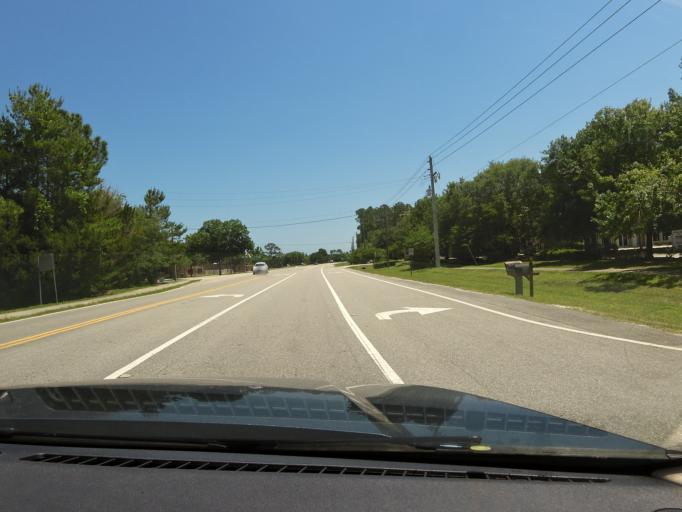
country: US
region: Florida
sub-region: Flagler County
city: Flagler Beach
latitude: 29.4739
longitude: -81.1774
